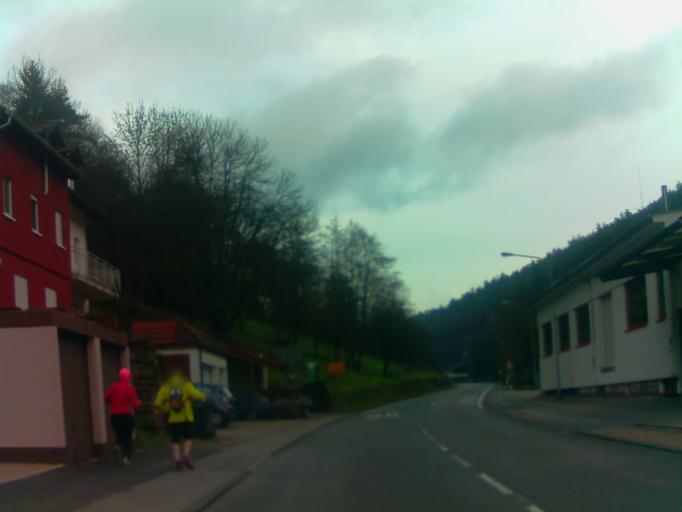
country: DE
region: Hesse
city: Hirschhorn
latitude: 49.4552
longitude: 8.8950
